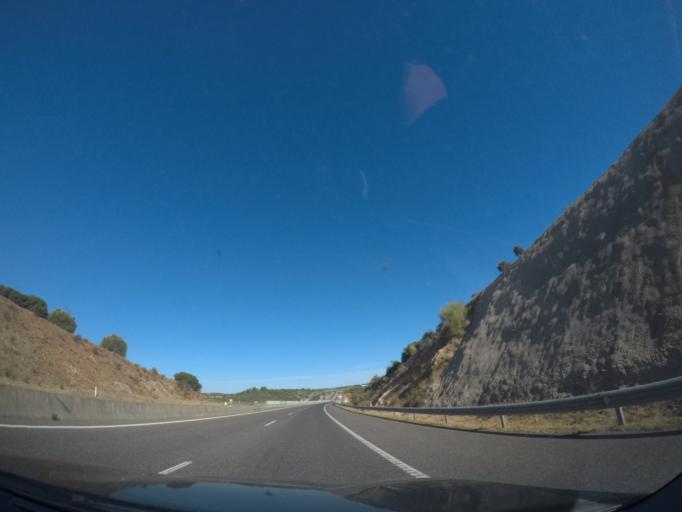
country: PT
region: Faro
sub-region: Portimao
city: Alvor
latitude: 37.1765
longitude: -8.5751
